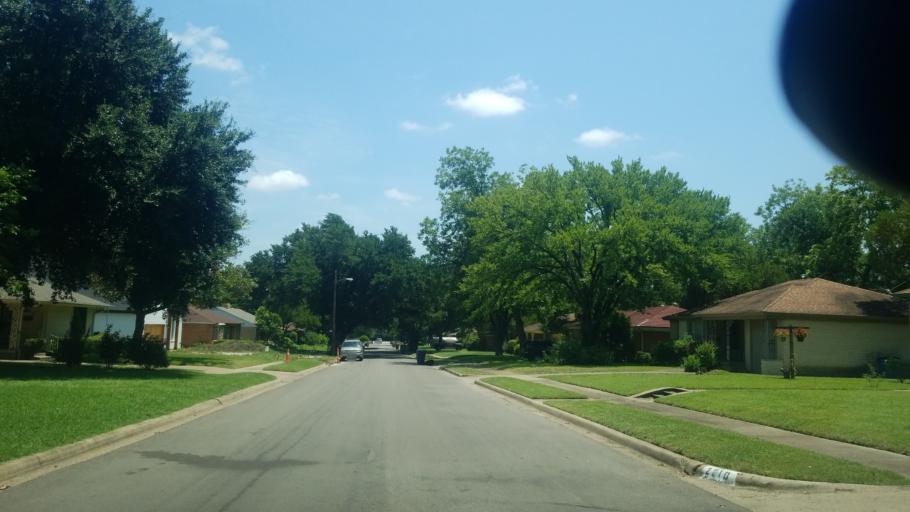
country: US
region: Texas
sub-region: Dallas County
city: Dallas
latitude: 32.7193
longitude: -96.7875
